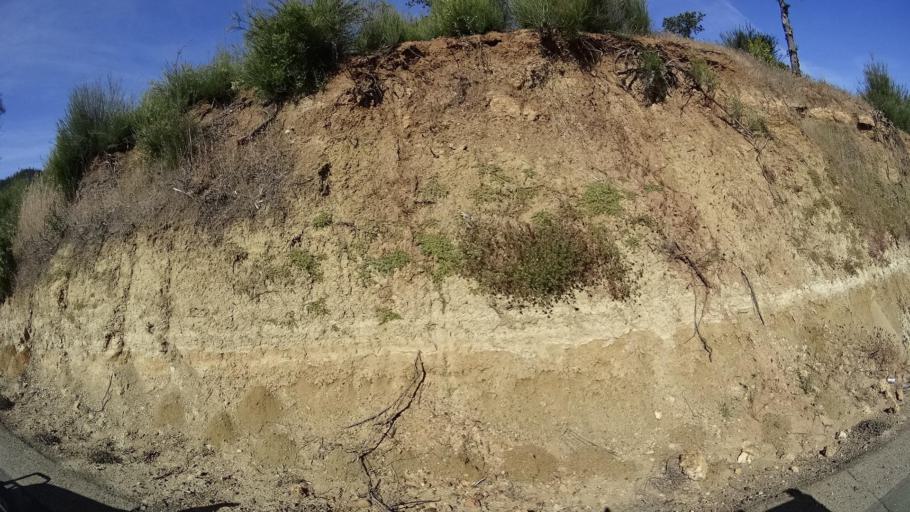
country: US
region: California
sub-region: Lake County
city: Kelseyville
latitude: 38.9396
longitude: -122.8153
